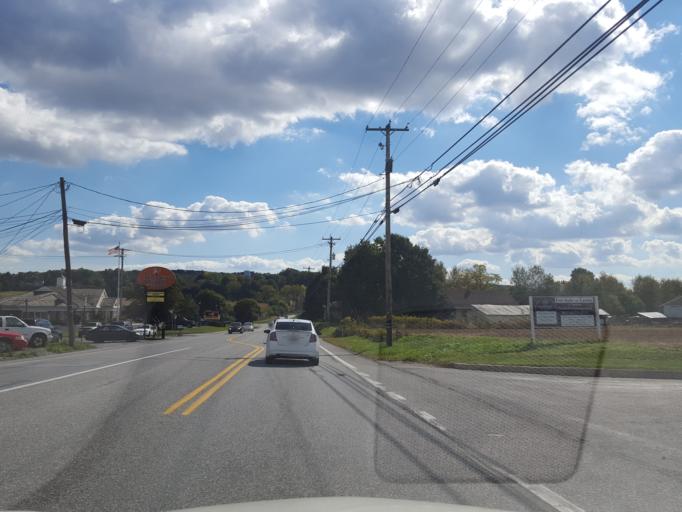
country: US
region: Pennsylvania
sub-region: York County
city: Yoe
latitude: 39.9426
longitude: -76.6454
